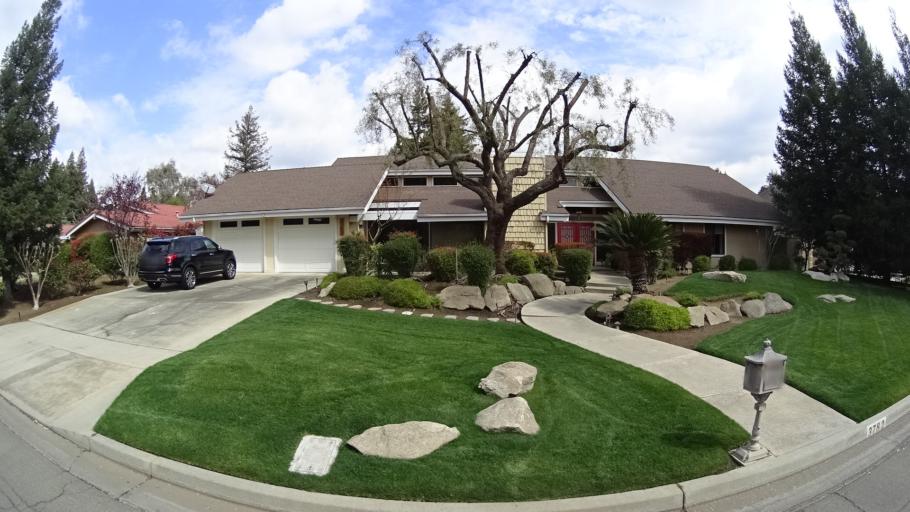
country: US
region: California
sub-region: Fresno County
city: Fresno
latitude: 36.8403
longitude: -119.8622
